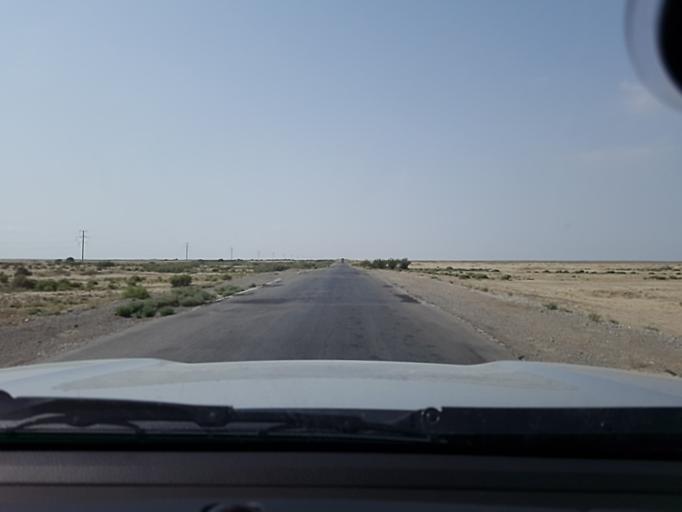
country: TM
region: Balkan
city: Gumdag
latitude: 38.9721
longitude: 54.5878
